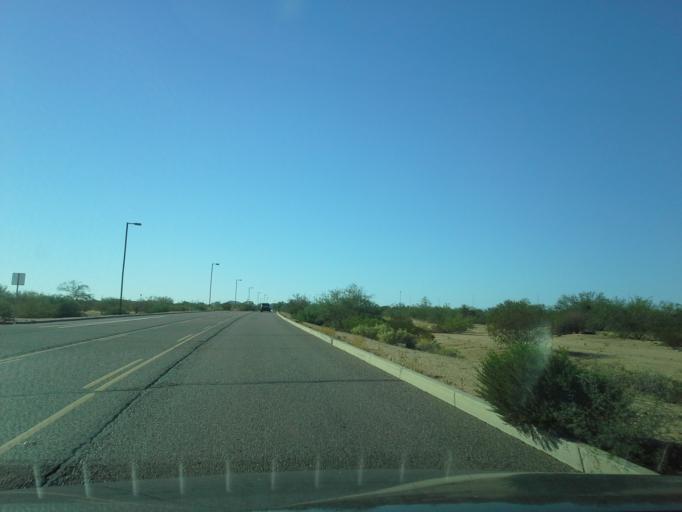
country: US
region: Arizona
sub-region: Maricopa County
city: Paradise Valley
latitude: 33.6598
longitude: -111.9497
